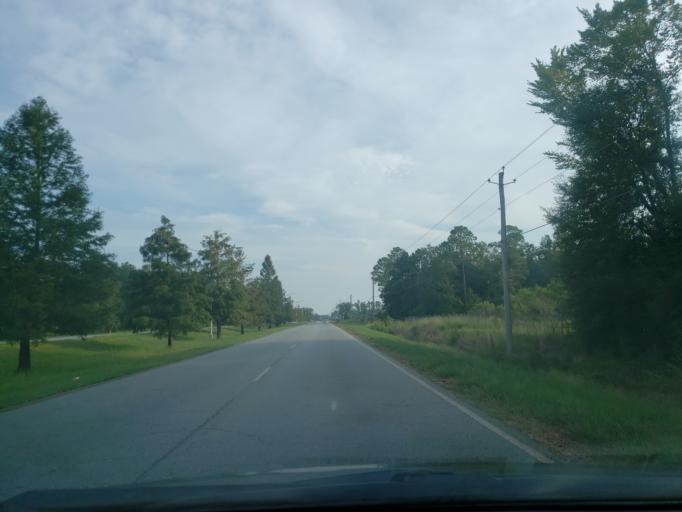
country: US
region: Georgia
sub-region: Dougherty County
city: Albany
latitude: 31.5806
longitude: -84.2193
